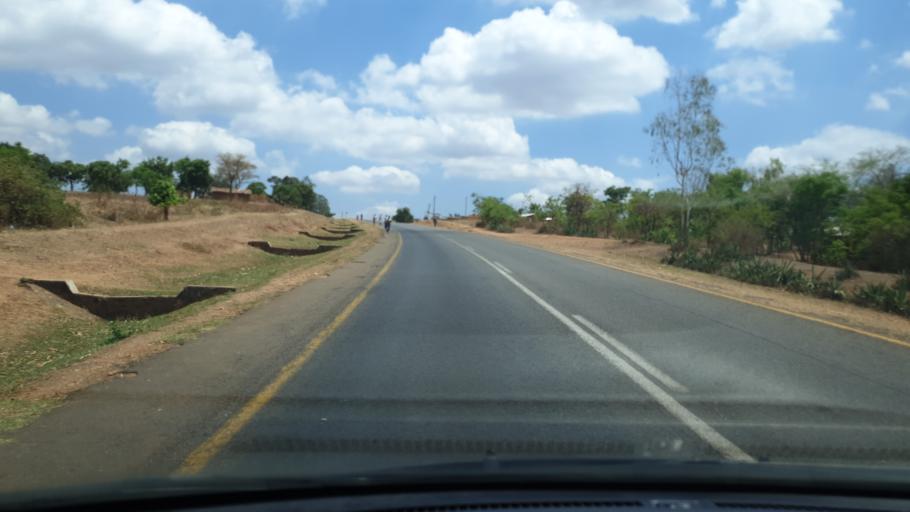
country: MW
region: Central Region
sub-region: Dowa District
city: Dowa
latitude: -13.7692
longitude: 34.0121
